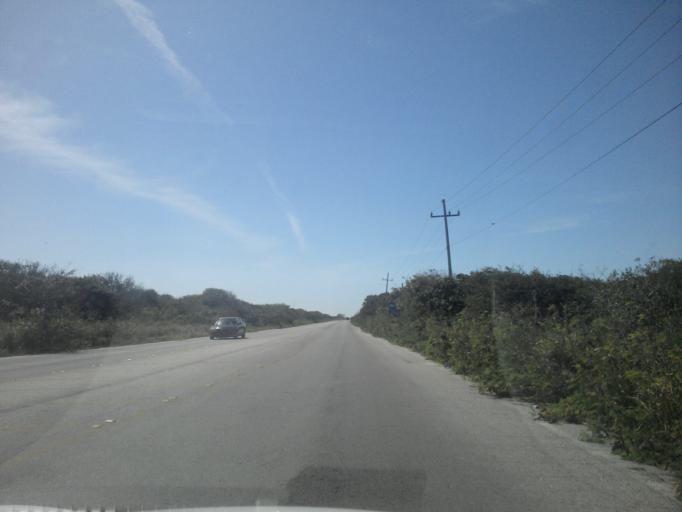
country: MX
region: Yucatan
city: Telchac Puerto
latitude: 21.3331
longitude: -89.3500
